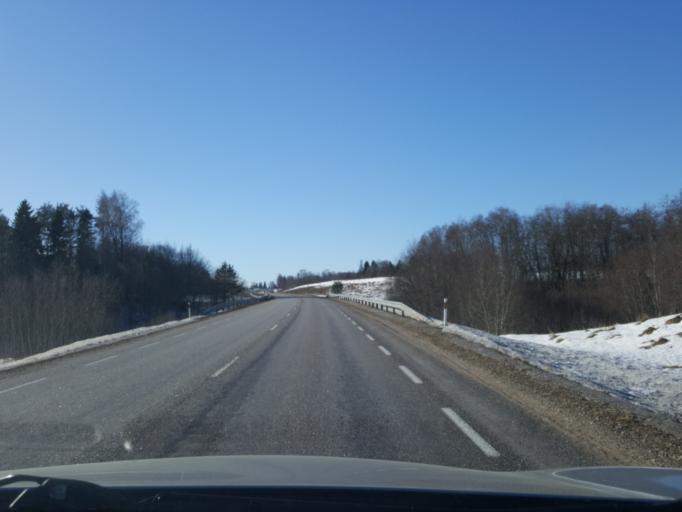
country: EE
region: Viljandimaa
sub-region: Viiratsi vald
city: Viiratsi
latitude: 58.4048
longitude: 25.6600
